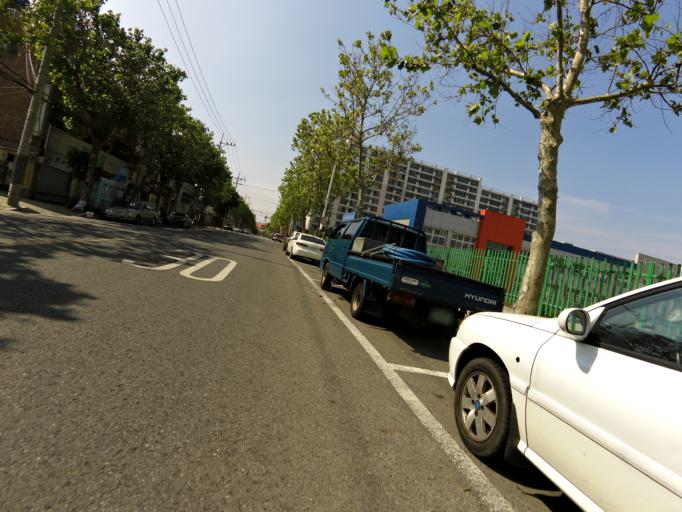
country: KR
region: Daegu
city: Daegu
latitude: 35.8719
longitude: 128.6439
